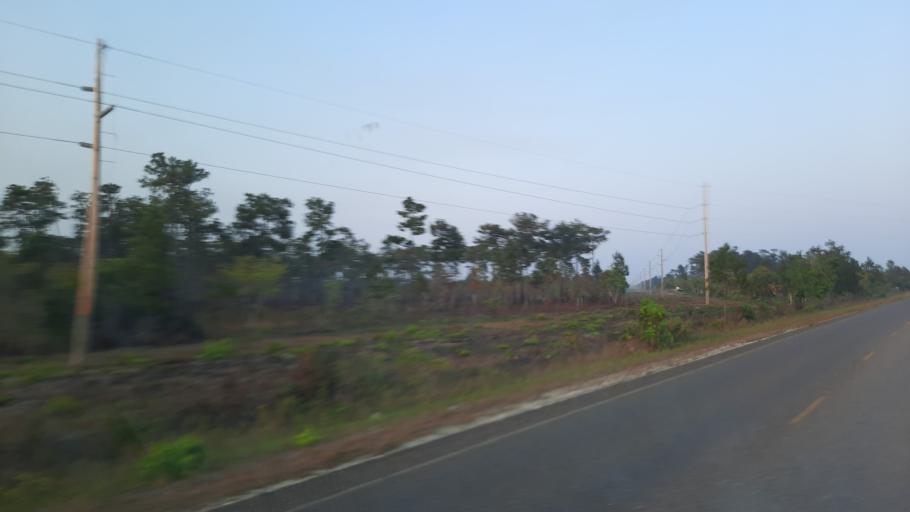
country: BZ
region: Stann Creek
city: Placencia
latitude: 16.5313
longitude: -88.4571
